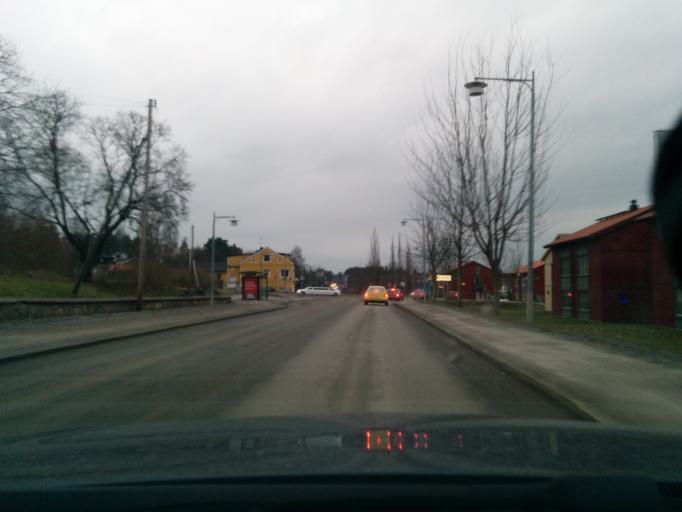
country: SE
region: Stockholm
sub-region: Taby Kommun
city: Taby
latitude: 59.4899
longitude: 18.0584
